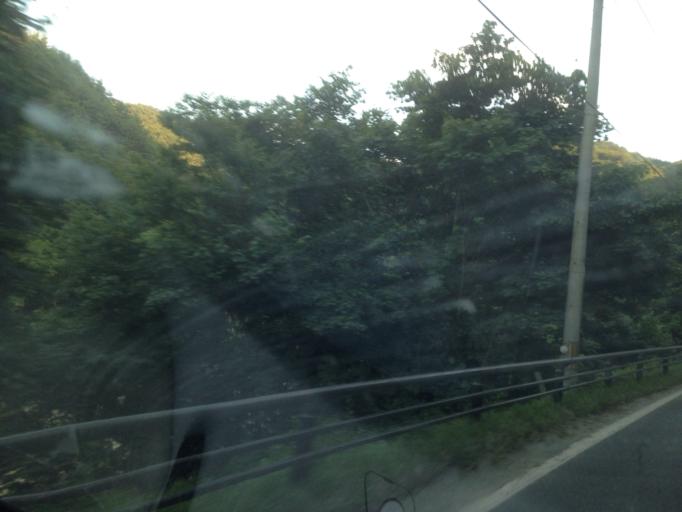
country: JP
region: Iwate
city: Kamaishi
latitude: 39.2968
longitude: 141.8837
